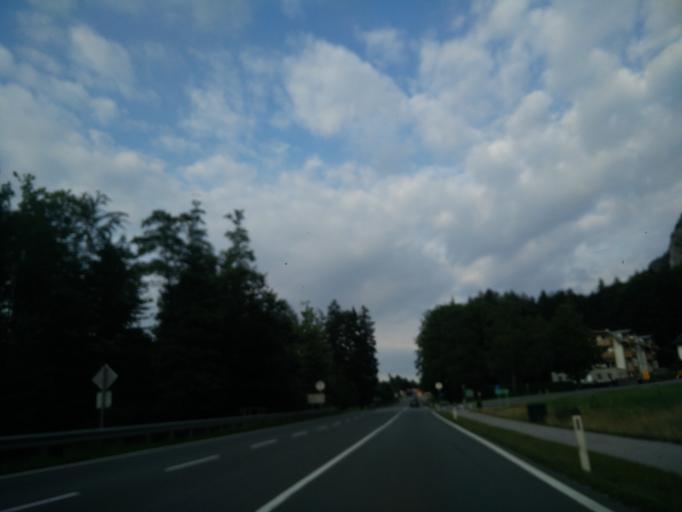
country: AT
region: Salzburg
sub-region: Politischer Bezirk Salzburg-Umgebung
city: Hallwang
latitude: 47.8198
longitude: 13.1050
